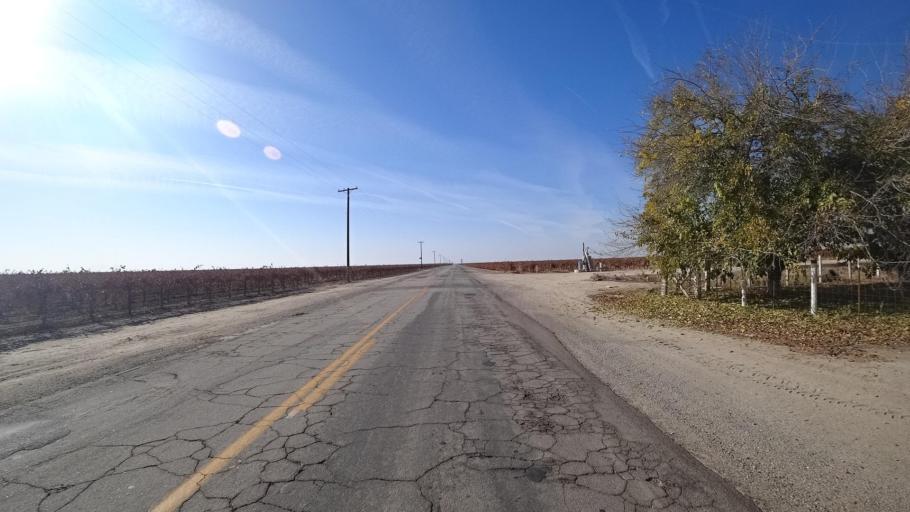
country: US
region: California
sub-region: Kern County
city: Wasco
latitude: 35.7031
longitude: -119.3844
